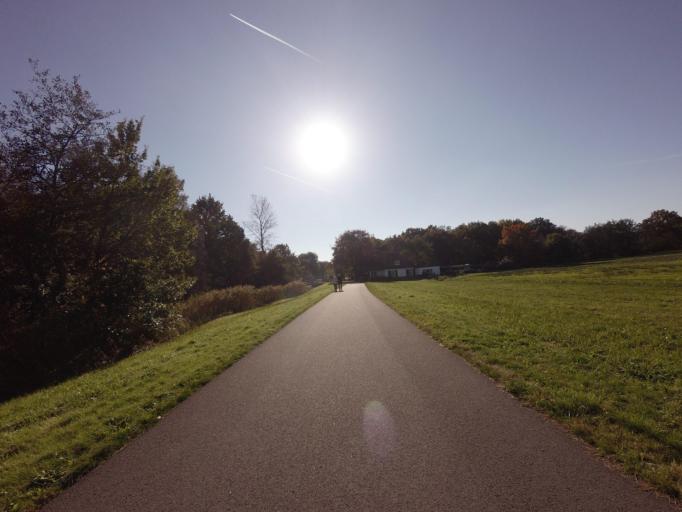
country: NL
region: North Holland
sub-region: Gemeente Naarden
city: Naarden
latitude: 52.2864
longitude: 5.1429
